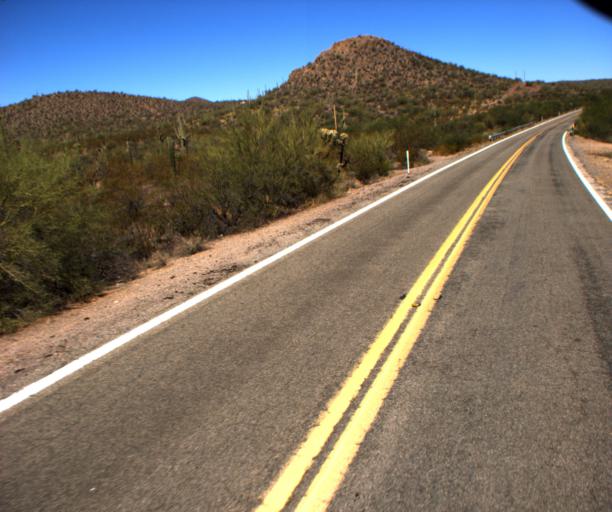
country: US
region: Arizona
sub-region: Pima County
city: Sells
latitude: 32.1705
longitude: -112.1483
